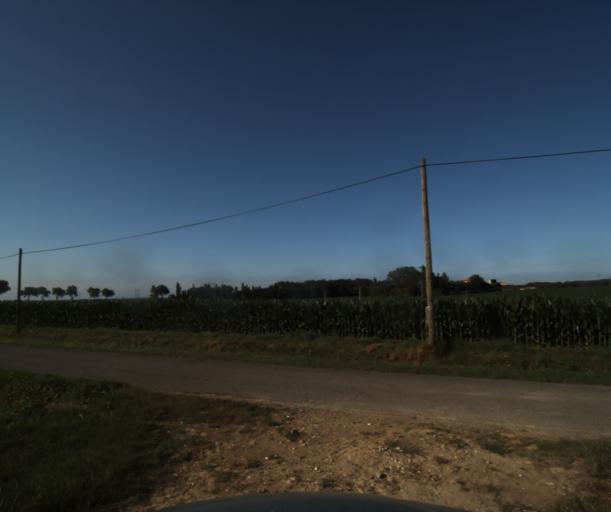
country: FR
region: Midi-Pyrenees
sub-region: Departement de la Haute-Garonne
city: Labarthe-sur-Leze
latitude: 43.4443
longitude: 1.3807
